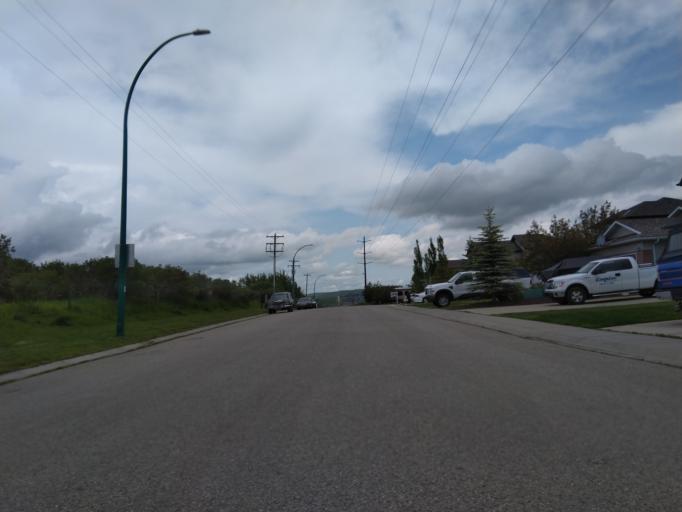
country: CA
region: Alberta
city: Cochrane
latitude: 51.1848
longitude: -114.5133
